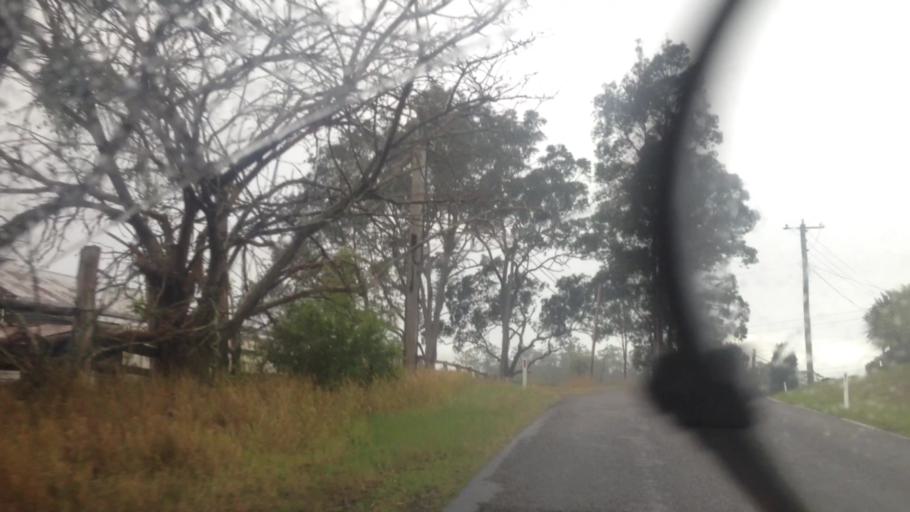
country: AU
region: New South Wales
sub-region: Wyong Shire
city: Little Jilliby
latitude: -33.1969
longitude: 151.3600
